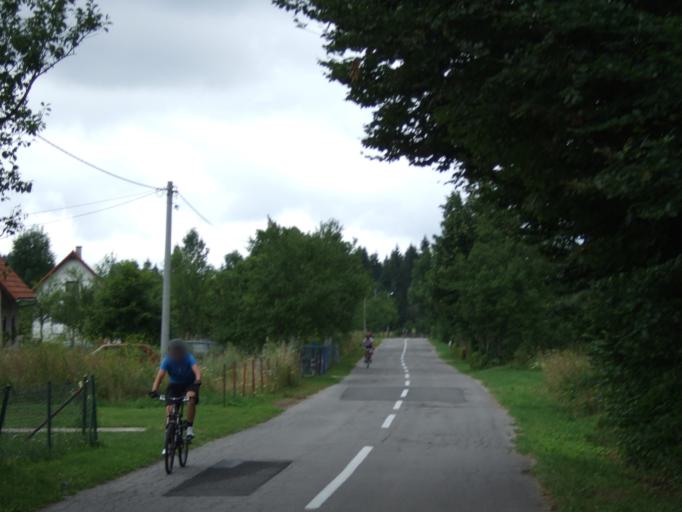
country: HR
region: Licko-Senjska
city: Jezerce
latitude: 44.9491
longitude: 15.5347
